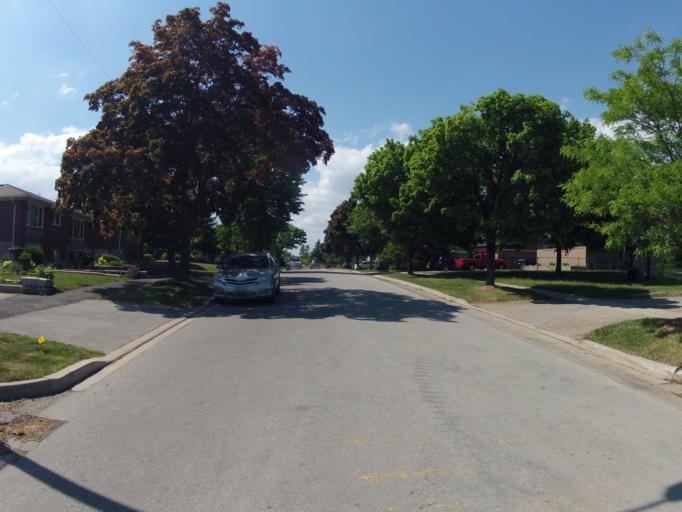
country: CA
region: Ontario
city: Oakville
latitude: 43.5088
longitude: -79.6474
